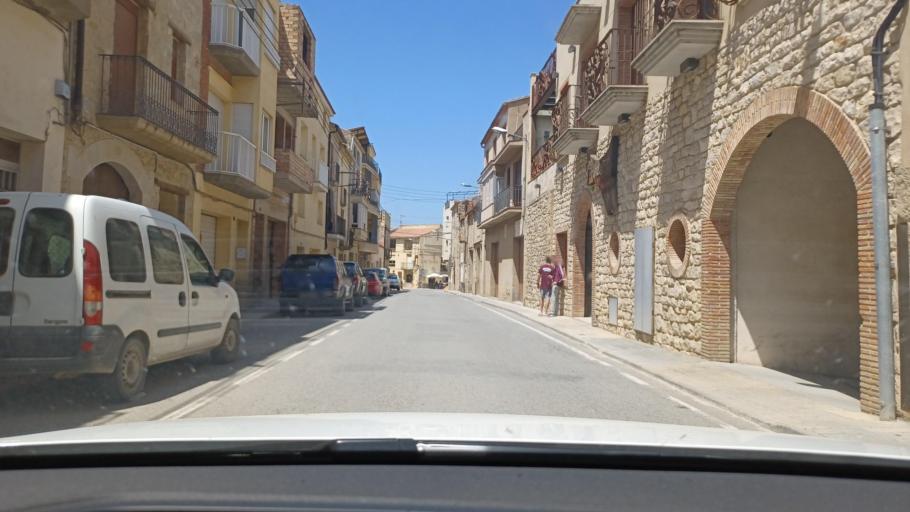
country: ES
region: Catalonia
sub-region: Provincia de Tarragona
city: Vilalba dels Arcs
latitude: 41.1198
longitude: 0.4089
